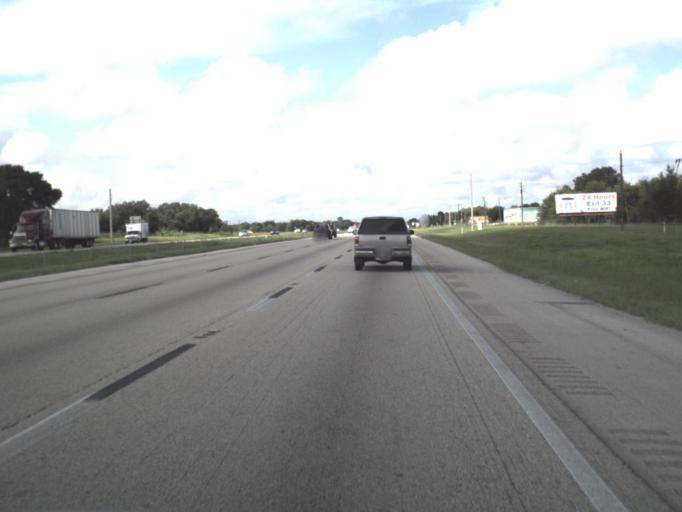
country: US
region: Florida
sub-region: Polk County
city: Gibsonia
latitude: 28.1309
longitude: -81.9191
